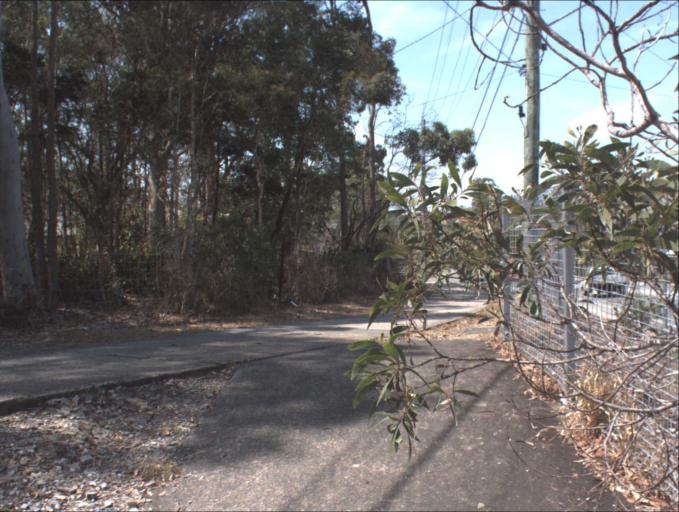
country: AU
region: Queensland
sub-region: Logan
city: Beenleigh
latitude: -27.6697
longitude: 153.2027
